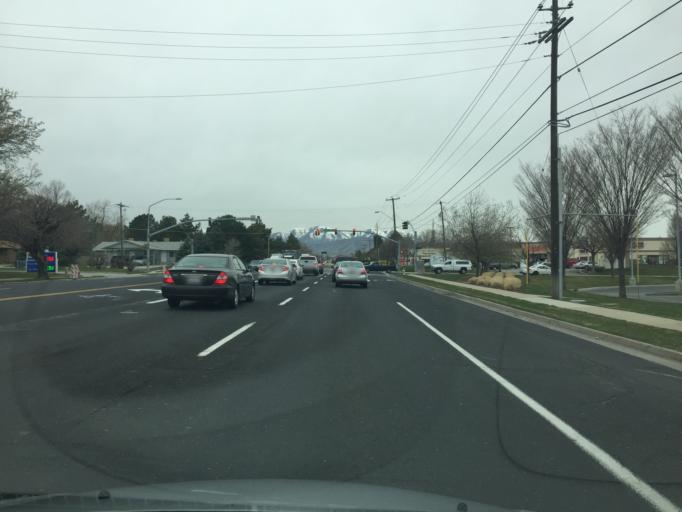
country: US
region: Utah
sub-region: Salt Lake County
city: Kearns
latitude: 40.6676
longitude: -111.9760
